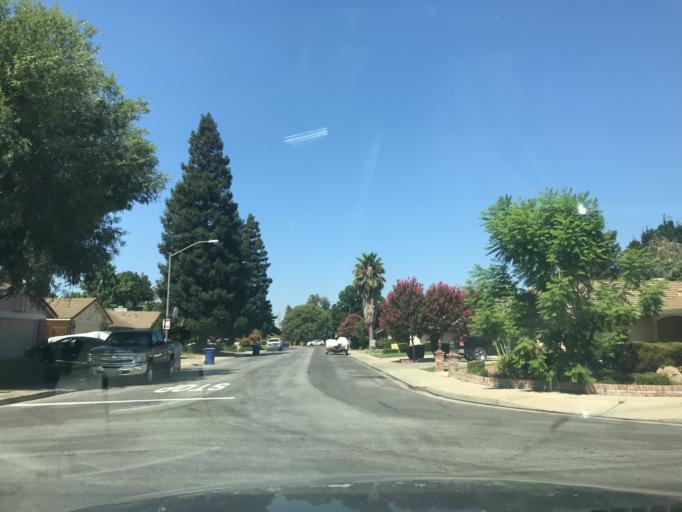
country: US
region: California
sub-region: Merced County
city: Merced
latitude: 37.3384
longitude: -120.4834
